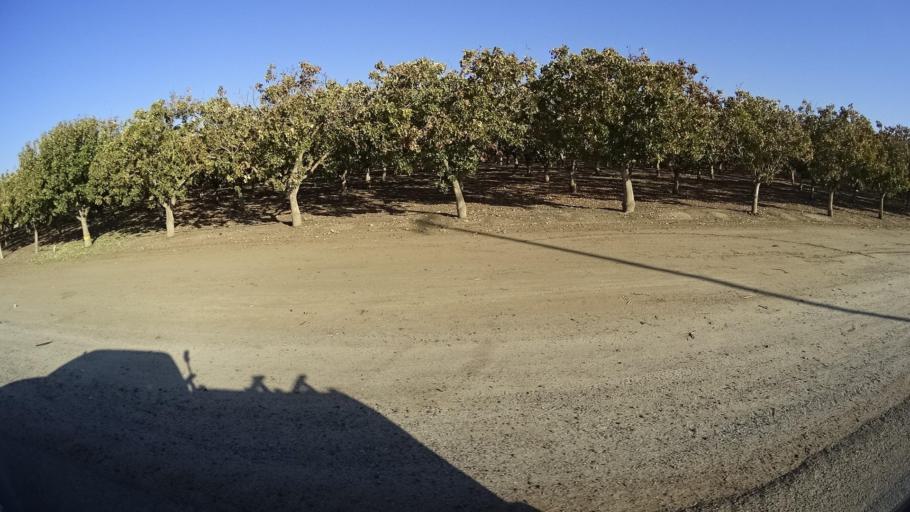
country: US
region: California
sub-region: Tulare County
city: Richgrove
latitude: 35.7906
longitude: -119.1689
